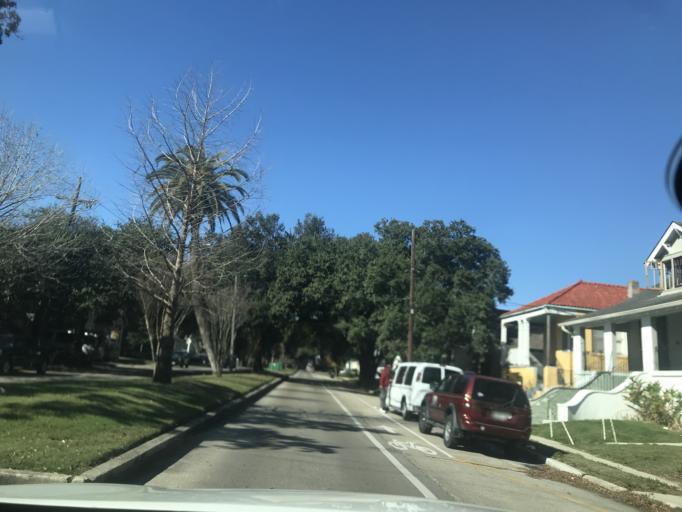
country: US
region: Louisiana
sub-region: Orleans Parish
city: New Orleans
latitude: 29.9500
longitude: -90.1061
